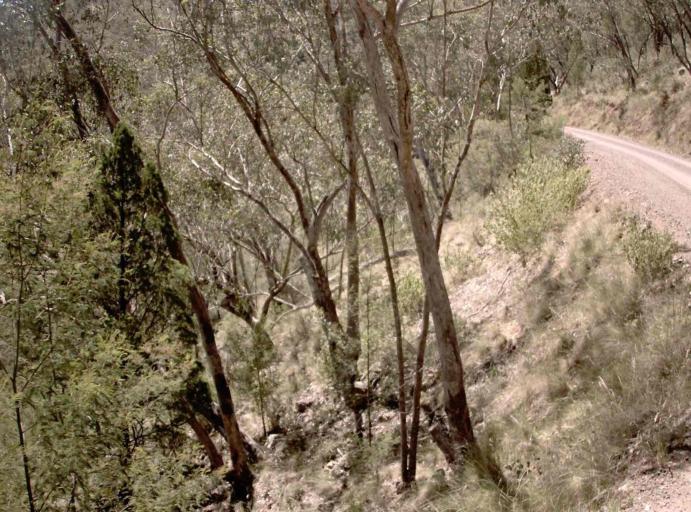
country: AU
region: New South Wales
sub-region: Snowy River
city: Jindabyne
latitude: -37.0657
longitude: 148.5047
